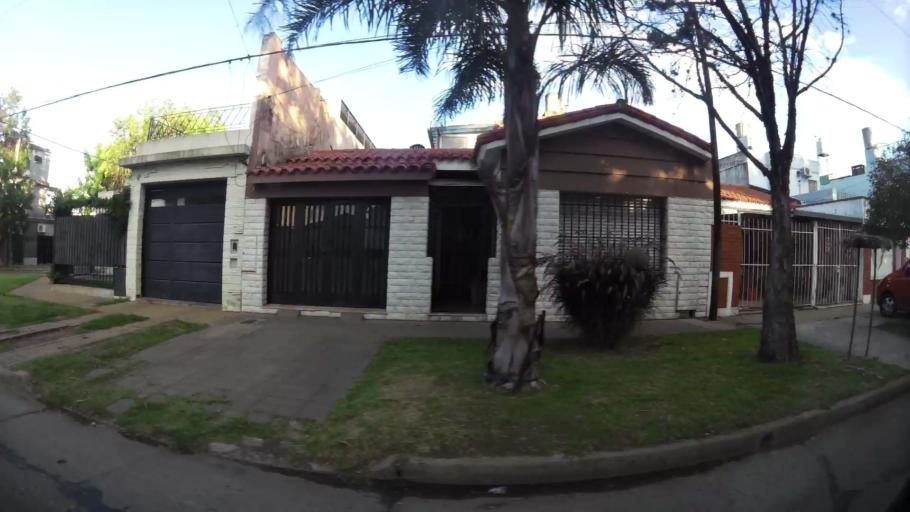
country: AR
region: Santa Fe
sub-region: Departamento de Rosario
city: Rosario
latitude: -32.9729
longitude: -60.6662
